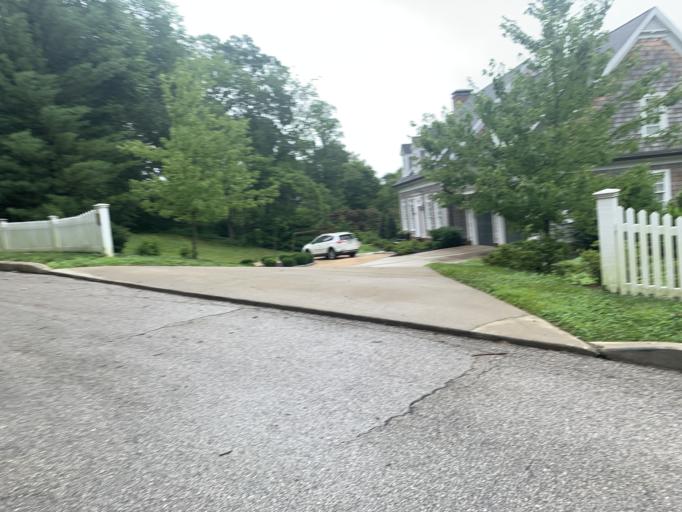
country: US
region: West Virginia
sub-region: Kanawha County
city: Charleston
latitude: 38.3407
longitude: -81.6413
